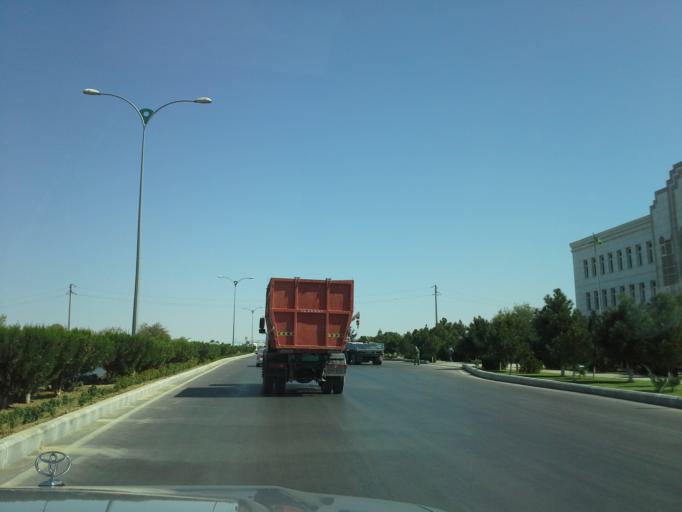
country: TM
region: Ahal
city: Annau
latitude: 37.9105
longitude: 58.5001
